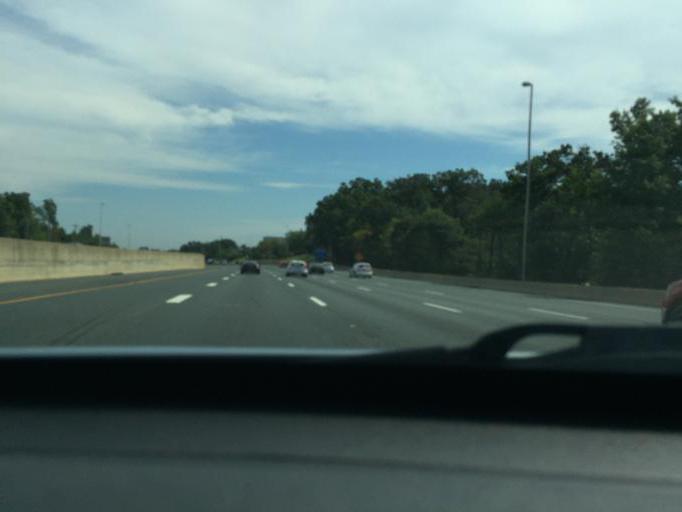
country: US
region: Virginia
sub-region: Prince William County
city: Sudley
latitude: 38.8017
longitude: -77.5141
